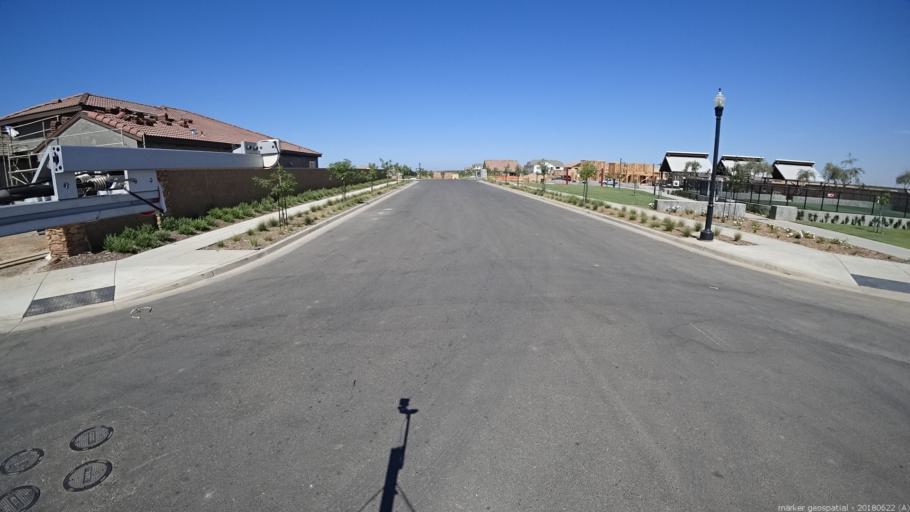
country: US
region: California
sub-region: Madera County
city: Bonadelle Ranchos-Madera Ranchos
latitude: 36.9165
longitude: -119.8018
